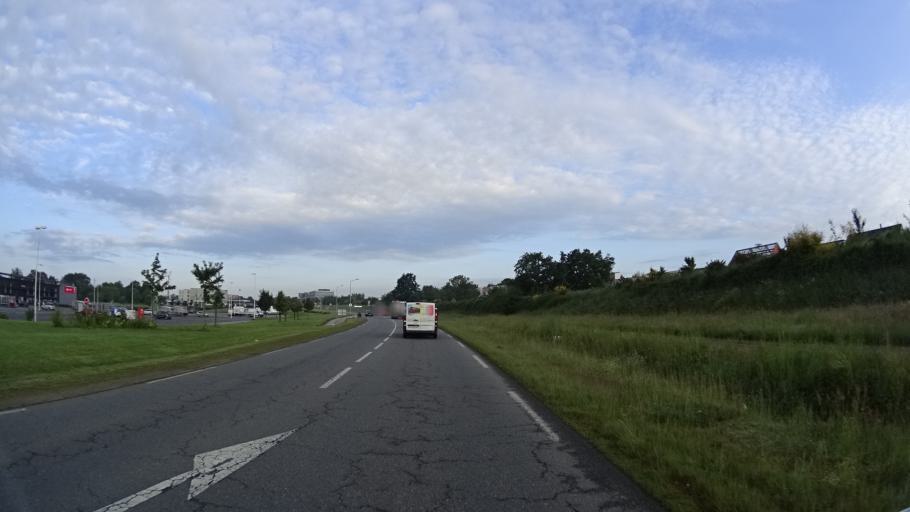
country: FR
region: Brittany
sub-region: Departement du Morbihan
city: Sene
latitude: 47.6439
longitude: -2.7392
